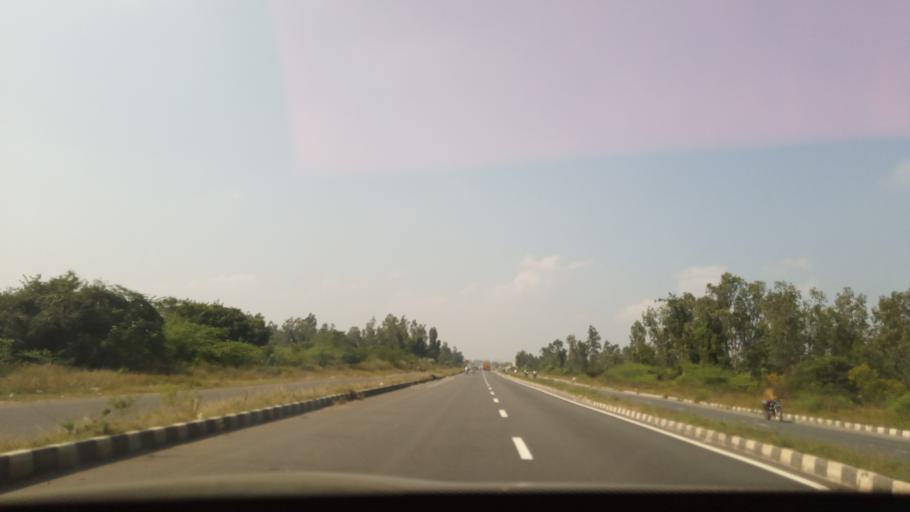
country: IN
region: Tamil Nadu
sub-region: Kancheepuram
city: Madambakkam
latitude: 12.8582
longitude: 79.9572
